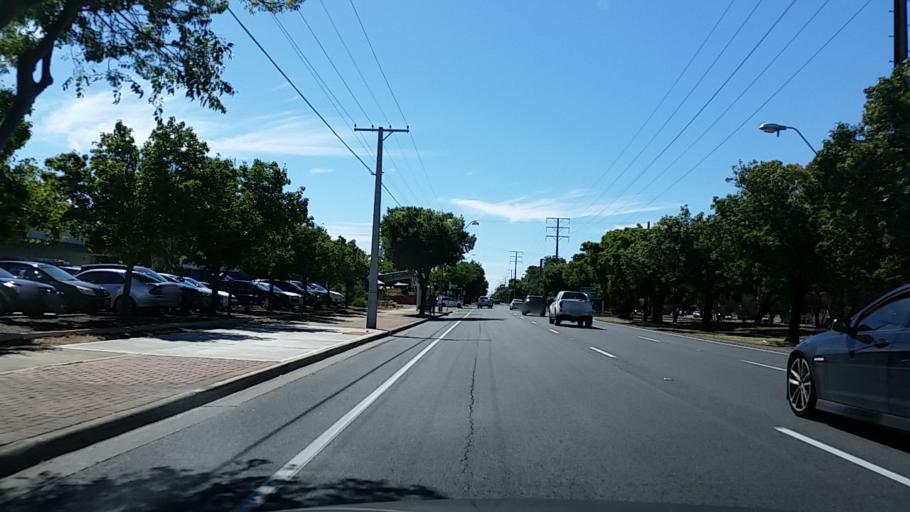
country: AU
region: South Australia
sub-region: Charles Sturt
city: Allenby Gardens
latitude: -34.8957
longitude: 138.5571
